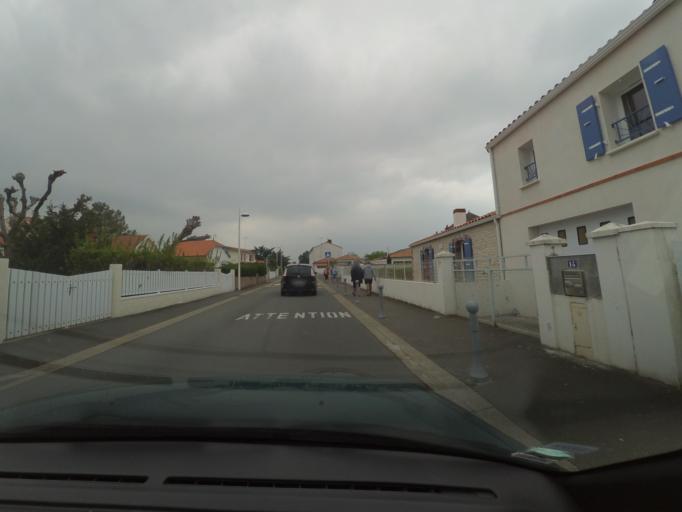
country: FR
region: Pays de la Loire
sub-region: Departement de la Vendee
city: Angles
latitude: 46.3309
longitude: -1.3216
